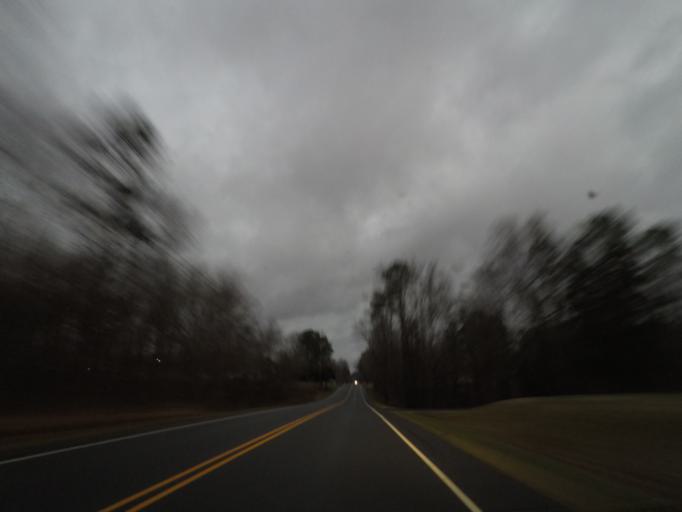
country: US
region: North Carolina
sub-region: Orange County
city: Hillsborough
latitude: 36.1123
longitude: -79.1116
